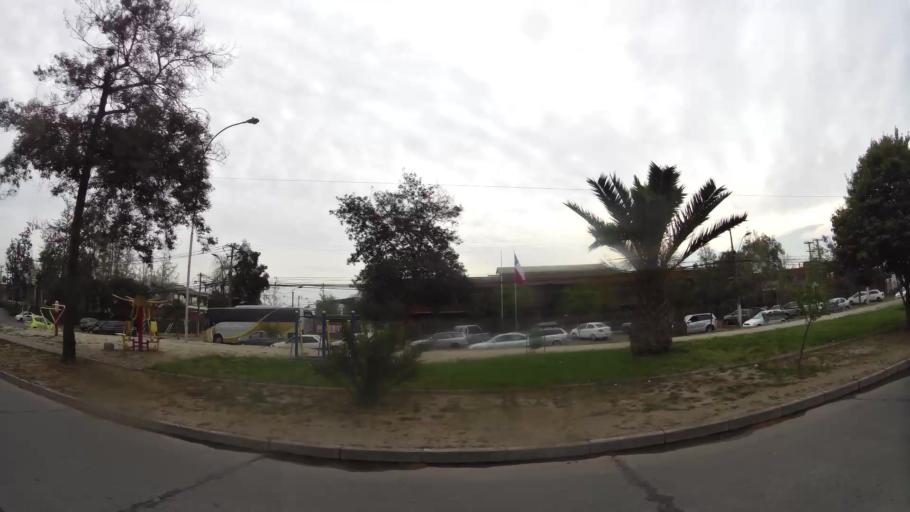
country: CL
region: Santiago Metropolitan
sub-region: Provincia de Santiago
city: Villa Presidente Frei, Nunoa, Santiago, Chile
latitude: -33.4780
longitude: -70.6132
